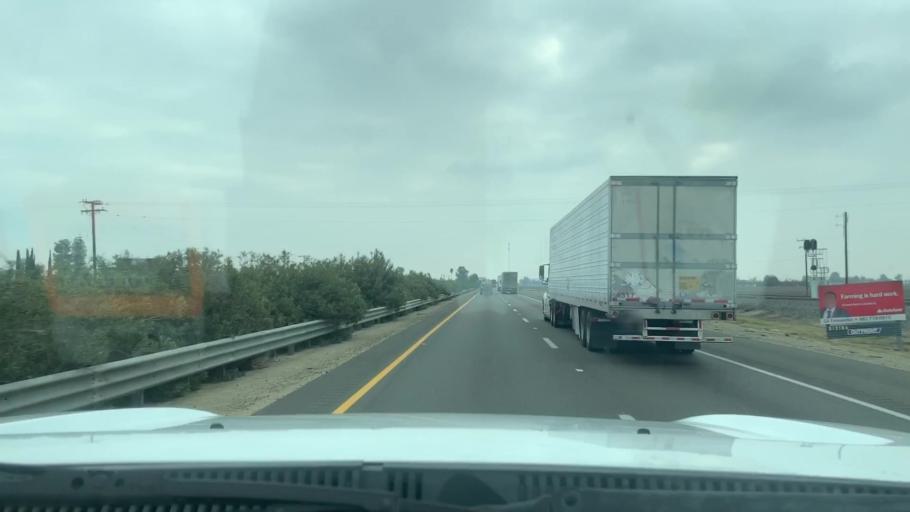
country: US
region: California
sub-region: Tulare County
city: Tipton
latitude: 36.0772
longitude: -119.3185
